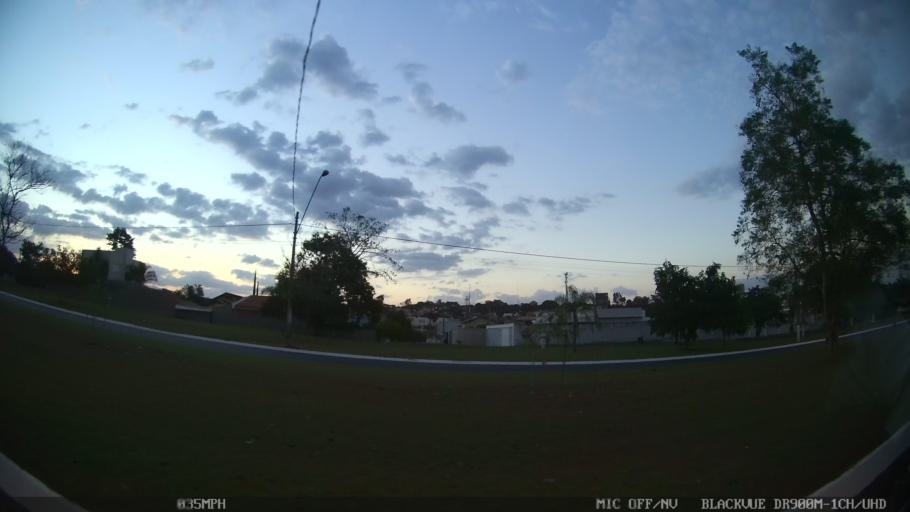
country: BR
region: Sao Paulo
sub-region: Ribeirao Preto
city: Ribeirao Preto
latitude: -21.2130
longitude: -47.7776
